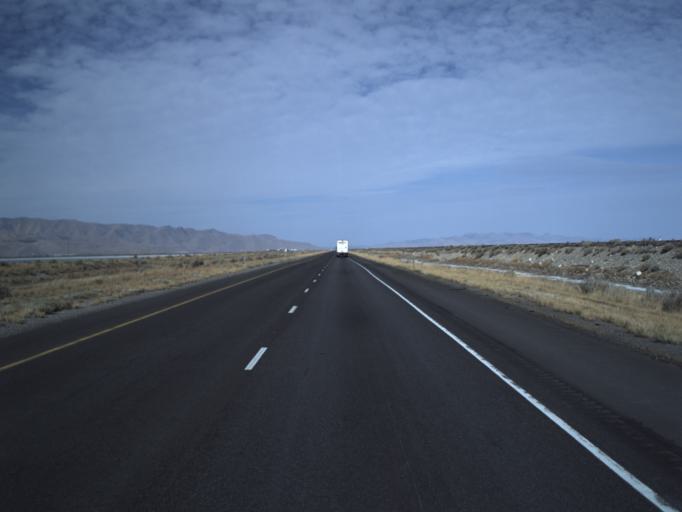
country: US
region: Utah
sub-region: Tooele County
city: Stansbury park
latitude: 40.6707
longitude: -112.3841
